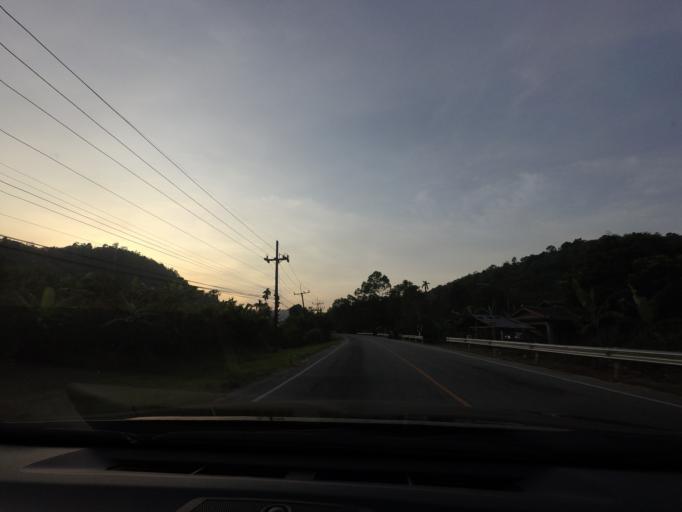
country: TH
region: Narathiwat
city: Yi-ngo
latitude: 6.3522
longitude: 101.6186
